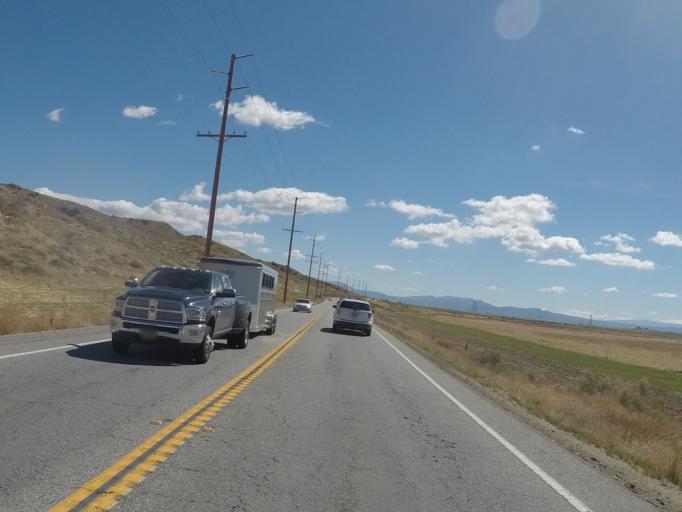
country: US
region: California
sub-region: Riverside County
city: Lakeview
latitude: 33.8768
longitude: -117.0534
